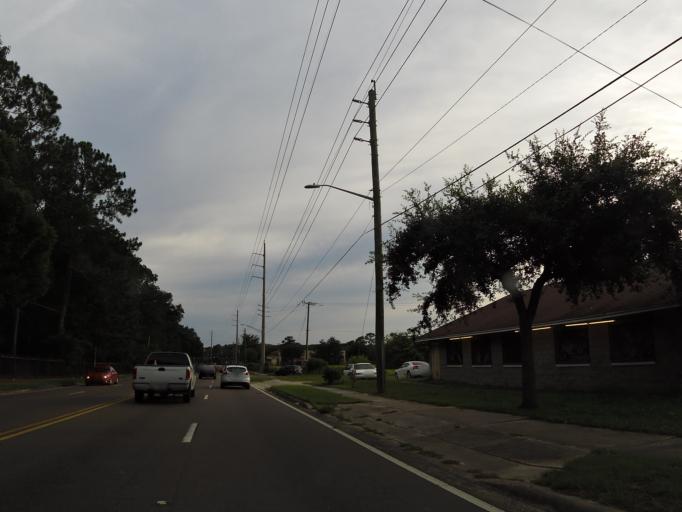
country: US
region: Florida
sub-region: Duval County
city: Jacksonville
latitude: 30.3941
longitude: -81.7287
